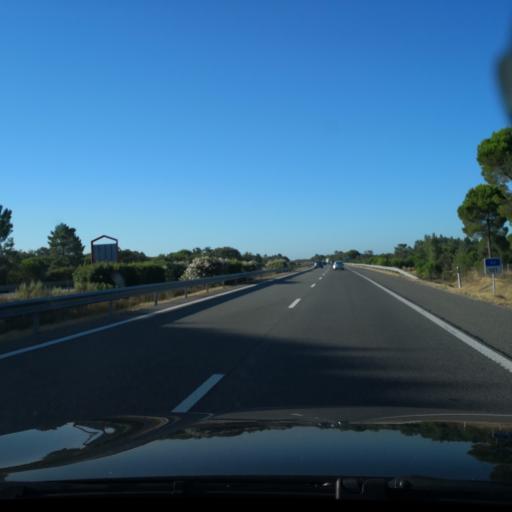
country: PT
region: Setubal
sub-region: Grandola
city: Grandola
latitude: 38.2032
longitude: -8.5136
